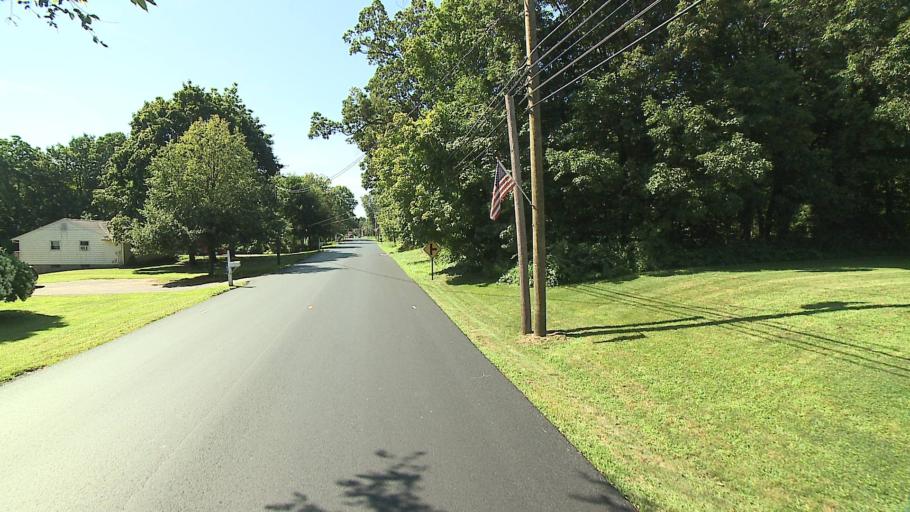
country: US
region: Connecticut
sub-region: Hartford County
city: Tariffville
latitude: 41.9522
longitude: -72.7236
